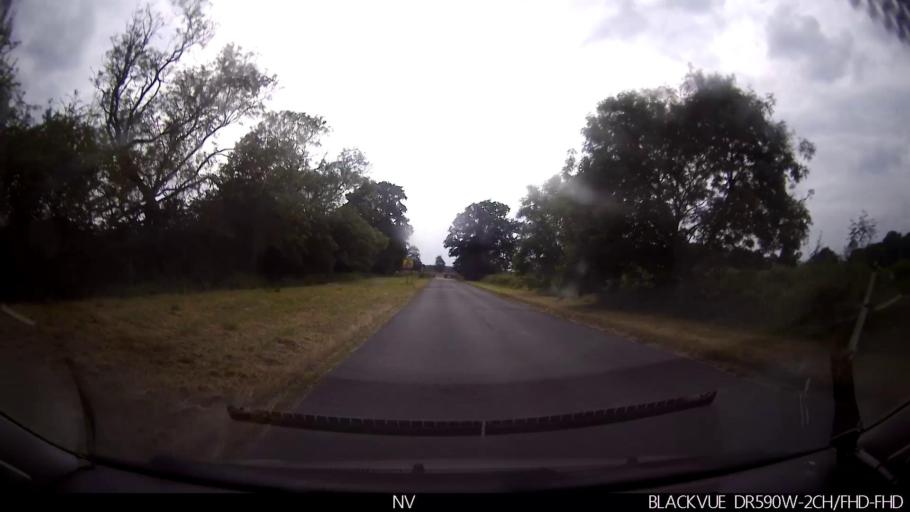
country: GB
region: England
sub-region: North Yorkshire
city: Strensall
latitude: 54.0461
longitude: -0.9919
